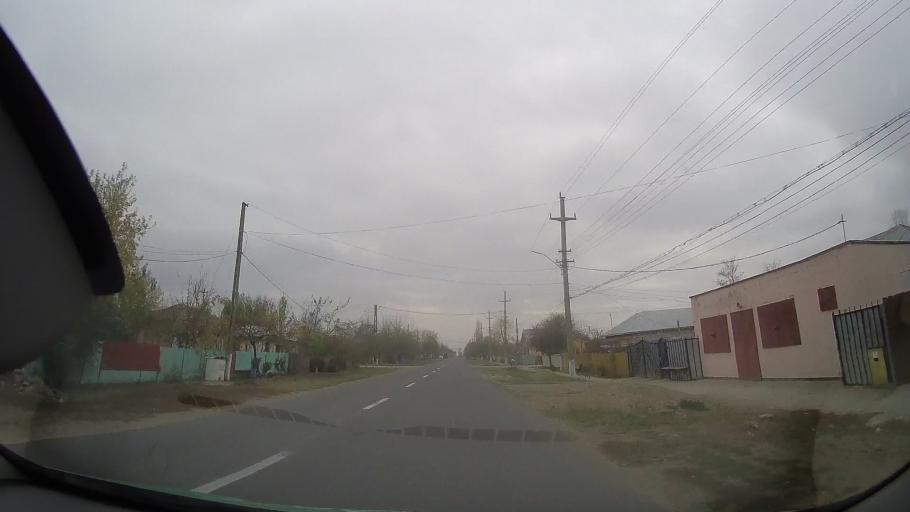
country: RO
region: Ialomita
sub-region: Comuna Garbovi
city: Garbovi
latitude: 44.7853
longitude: 26.7602
